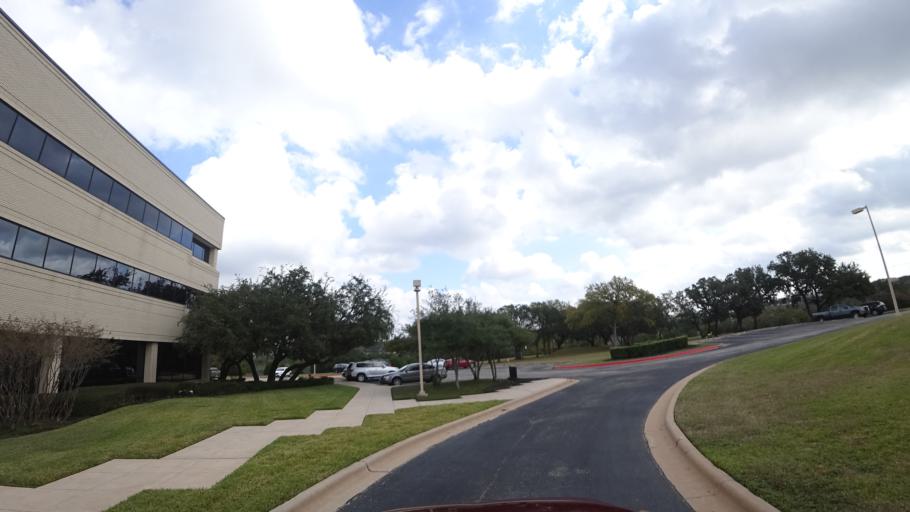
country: US
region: Texas
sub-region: Williamson County
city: Anderson Mill
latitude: 30.4227
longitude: -97.8518
